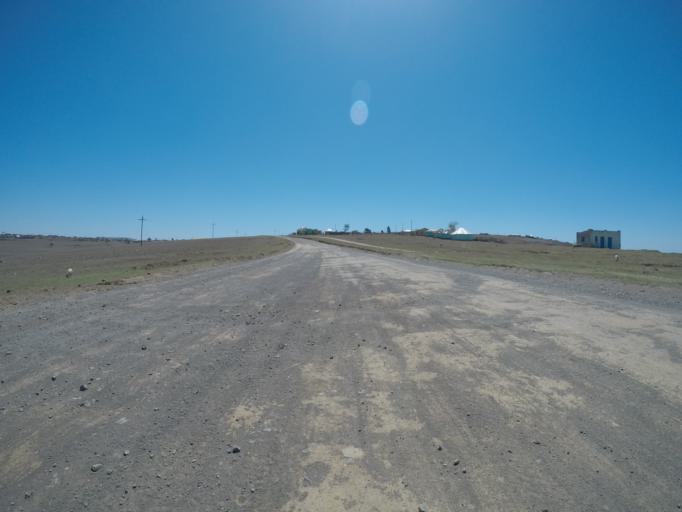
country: ZA
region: Eastern Cape
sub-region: OR Tambo District Municipality
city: Mthatha
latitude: -31.7880
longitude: 28.8158
